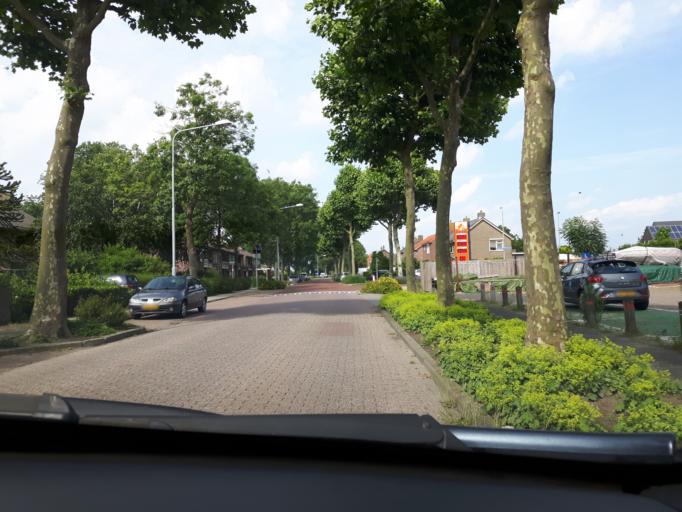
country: NL
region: Zeeland
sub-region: Gemeente Middelburg
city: Middelburg
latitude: 51.4837
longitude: 3.6595
